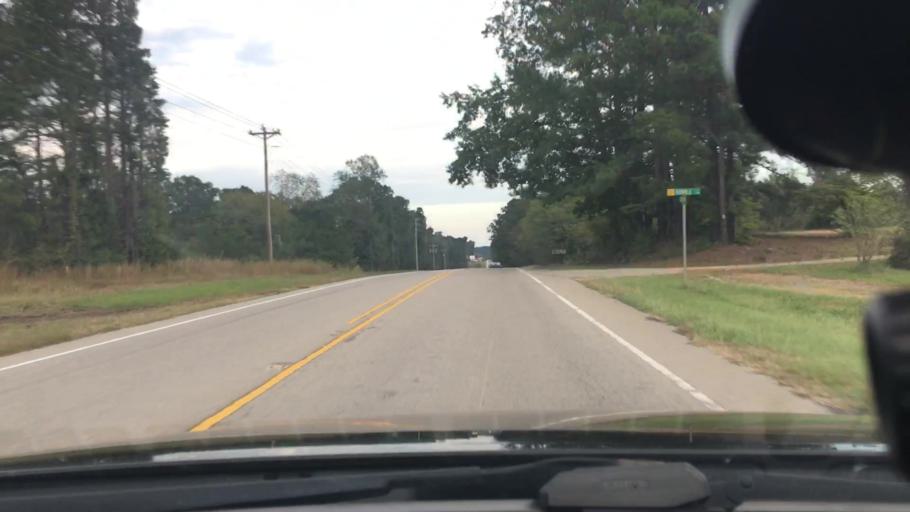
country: US
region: North Carolina
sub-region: Moore County
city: Robbins
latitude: 35.3886
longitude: -79.5063
